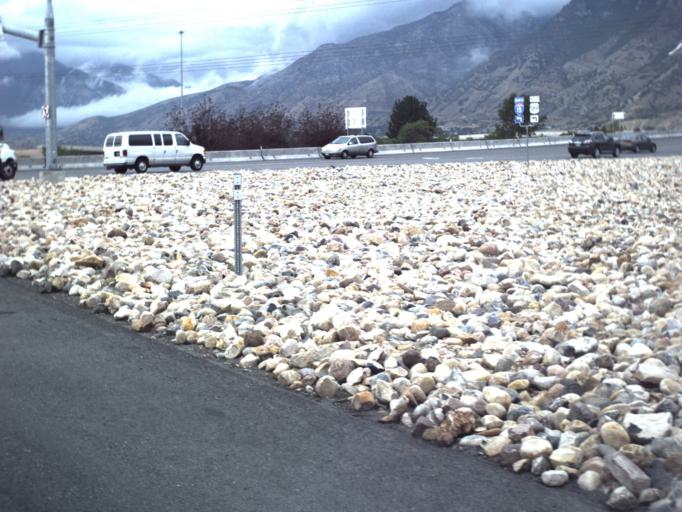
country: US
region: Utah
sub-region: Utah County
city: Provo
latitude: 40.2067
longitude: -111.6608
